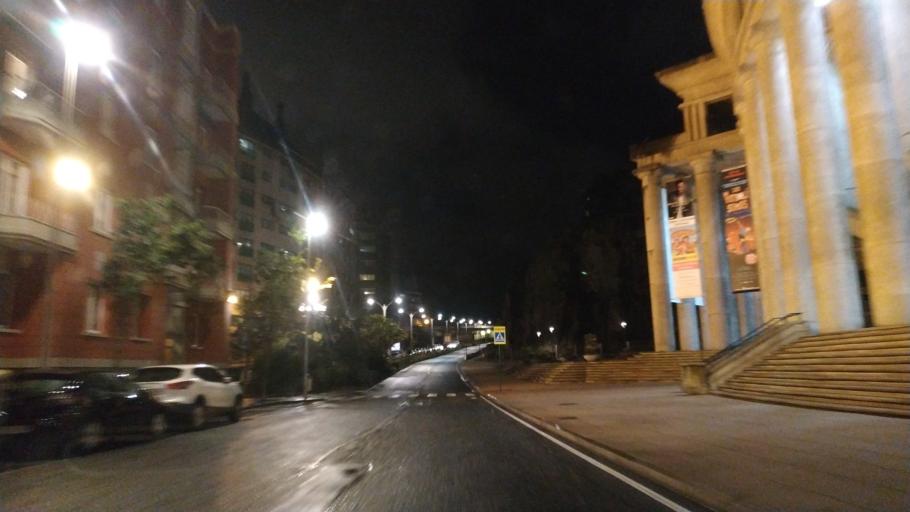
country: ES
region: Galicia
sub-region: Provincia da Coruna
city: A Coruna
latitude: 43.3632
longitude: -8.4104
